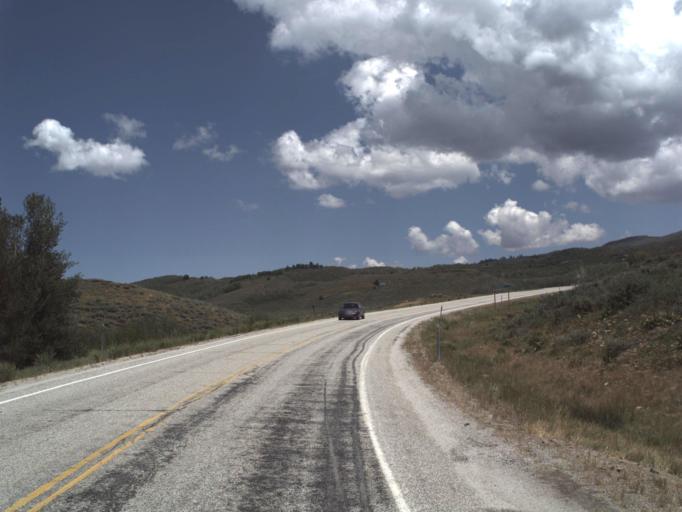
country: US
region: Utah
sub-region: Weber County
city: Wolf Creek
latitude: 41.4051
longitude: -111.5989
